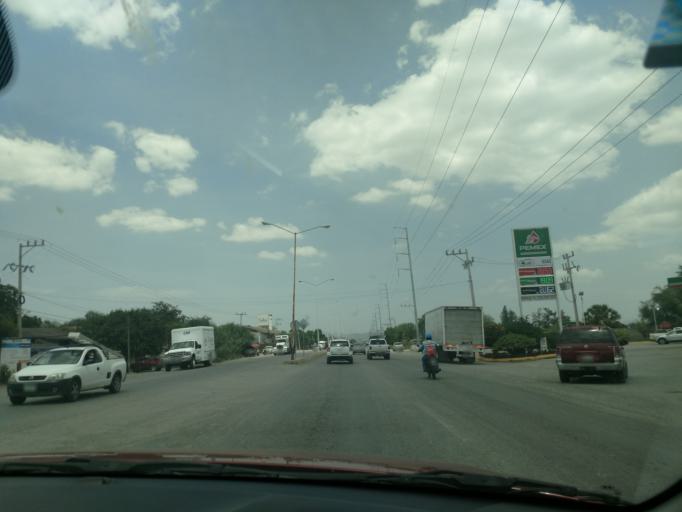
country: MX
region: San Luis Potosi
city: Rio Verde
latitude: 21.9223
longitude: -99.9777
